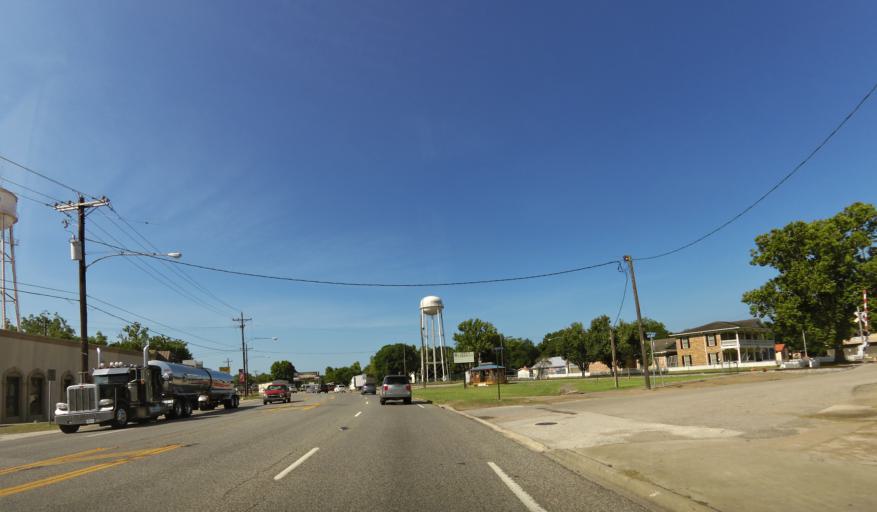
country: US
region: Texas
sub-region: Polk County
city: Corrigan
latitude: 30.9994
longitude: -94.8269
